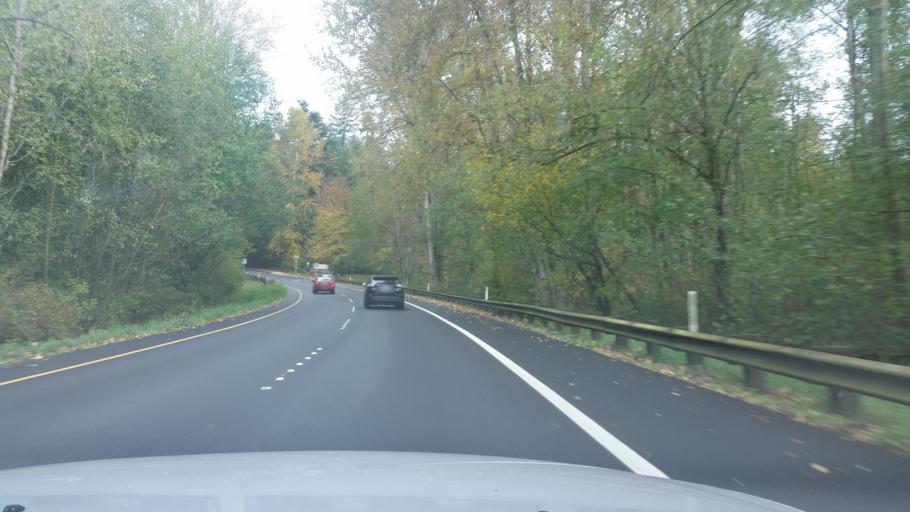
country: US
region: Washington
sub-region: King County
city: Eastgate
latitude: 47.5972
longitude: -122.1636
